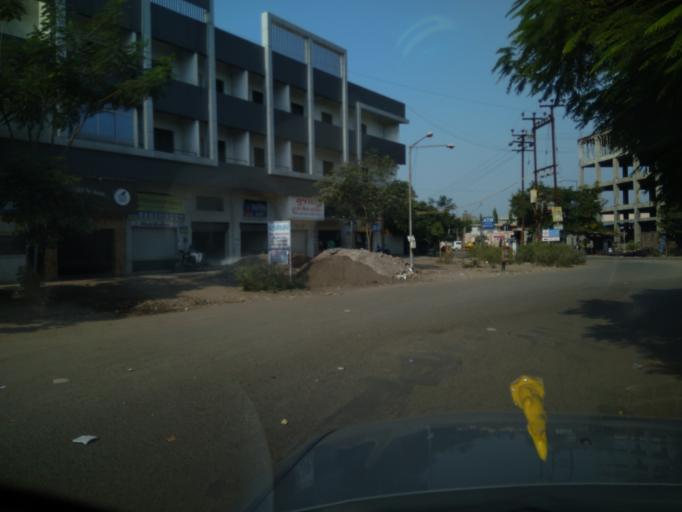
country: IN
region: Gujarat
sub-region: Jamnagar
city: Jamnagar
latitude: 22.4193
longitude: 70.0503
